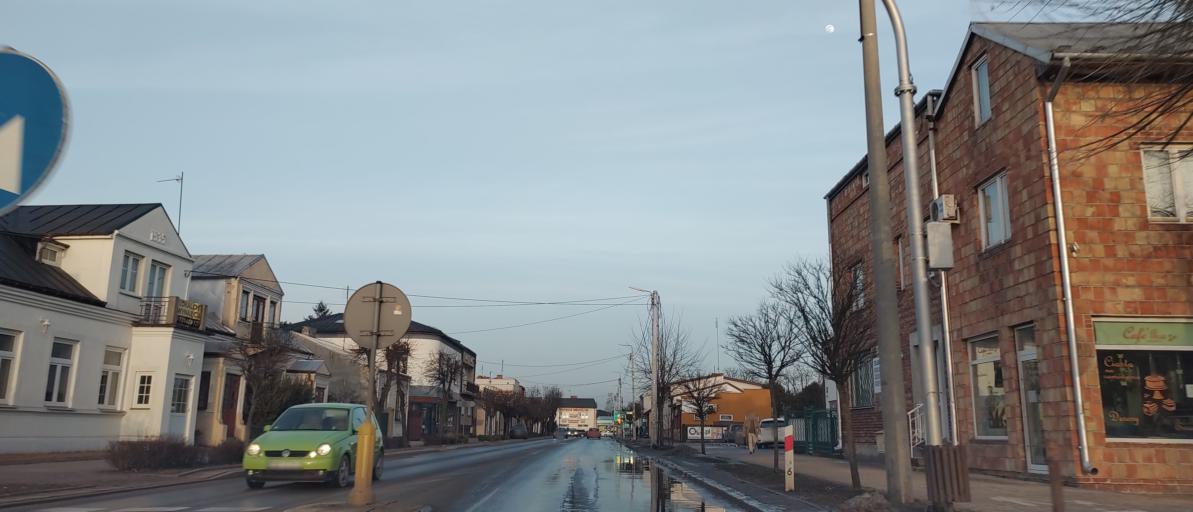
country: PL
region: Masovian Voivodeship
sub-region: Powiat bialobrzeski
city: Bialobrzegi
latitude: 51.6455
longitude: 20.9540
